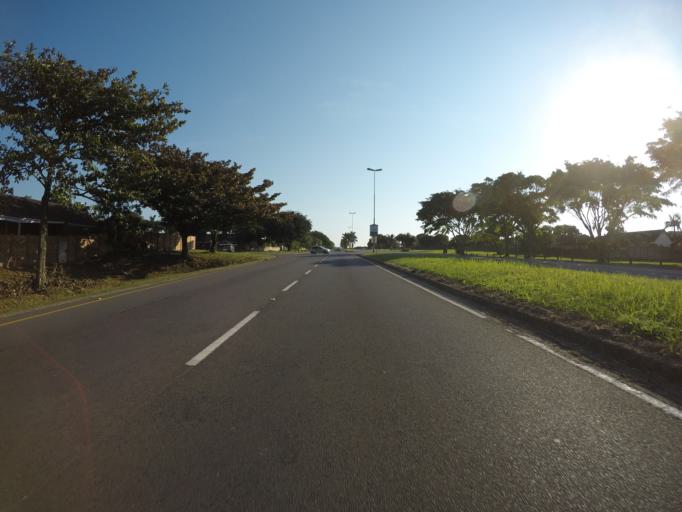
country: ZA
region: KwaZulu-Natal
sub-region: uThungulu District Municipality
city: Richards Bay
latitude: -28.7665
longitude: 32.0599
